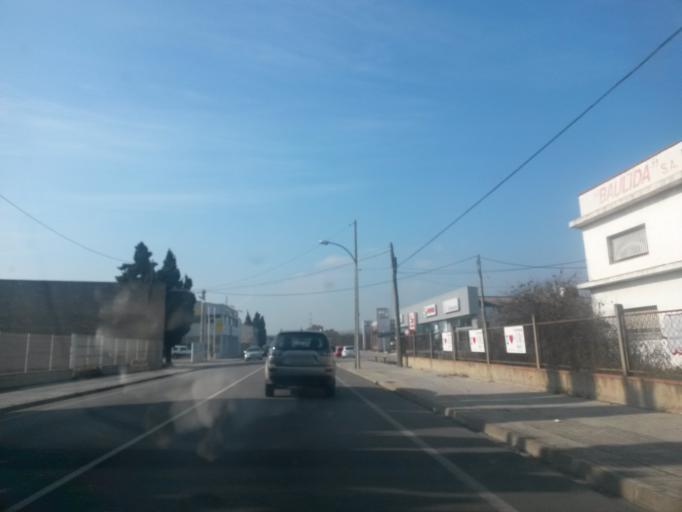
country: ES
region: Catalonia
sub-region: Provincia de Girona
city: Vilabertran
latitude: 42.2673
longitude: 2.9916
